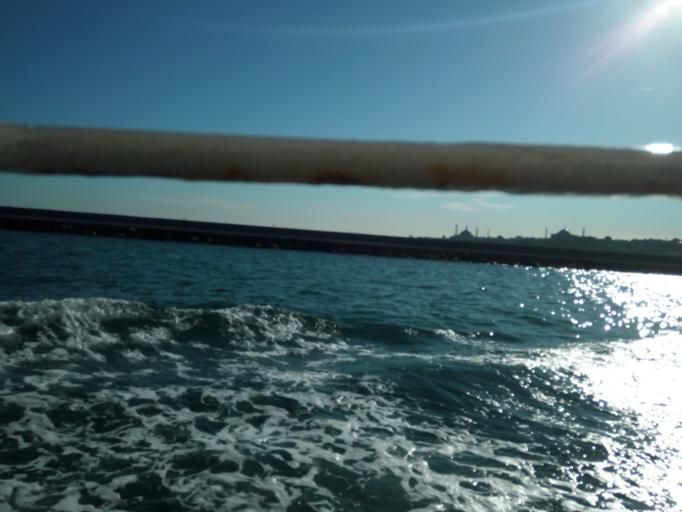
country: TR
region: Istanbul
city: UEskuedar
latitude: 41.0086
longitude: 29.0033
